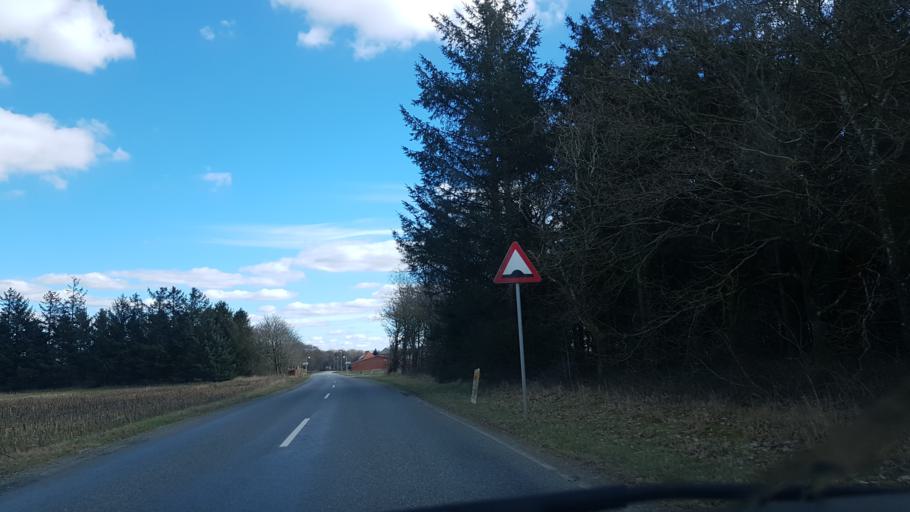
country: DK
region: South Denmark
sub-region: Esbjerg Kommune
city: Ribe
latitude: 55.4018
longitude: 8.7943
